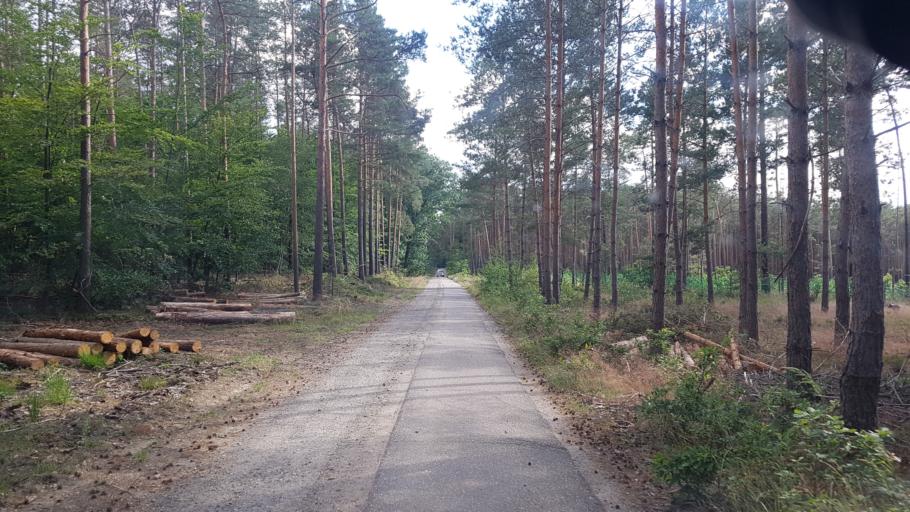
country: DE
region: Brandenburg
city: Trobitz
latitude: 51.6367
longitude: 13.4411
